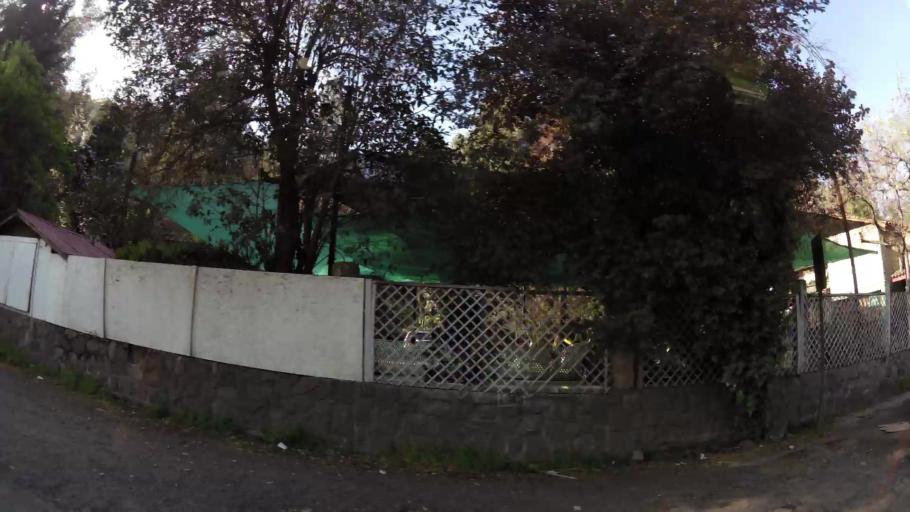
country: CL
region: Santiago Metropolitan
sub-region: Provincia de Santiago
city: Villa Presidente Frei, Nunoa, Santiago, Chile
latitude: -33.3620
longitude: -70.4941
